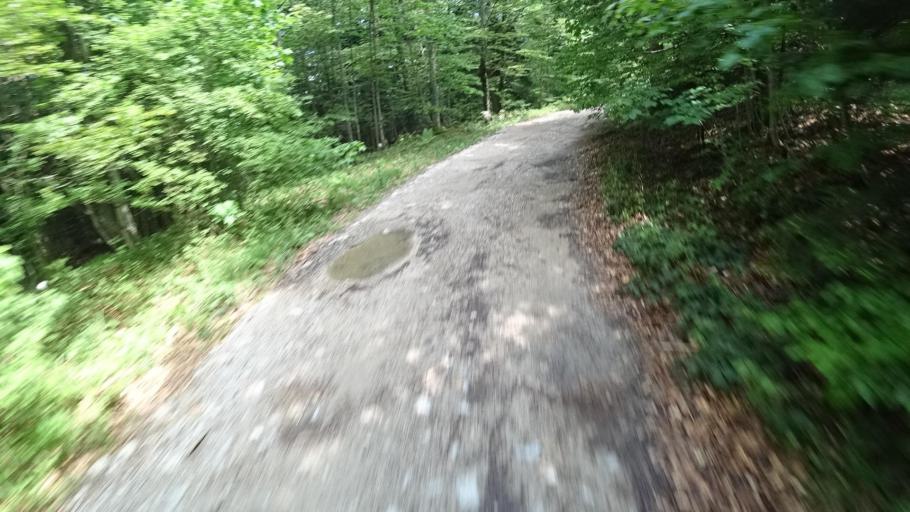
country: BA
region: Federation of Bosnia and Herzegovina
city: Bosanska Krupa
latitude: 44.7602
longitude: 16.1420
